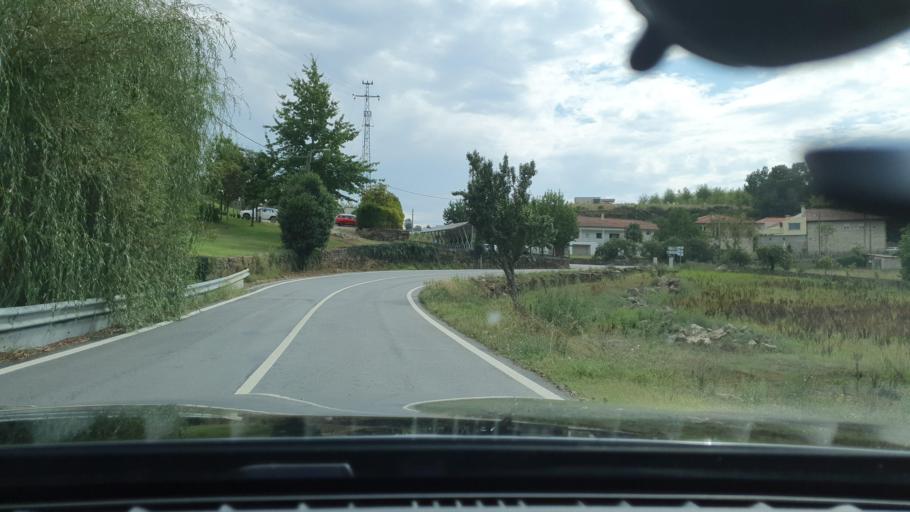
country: PT
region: Vila Real
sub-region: Boticas
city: Boticas
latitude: 41.7104
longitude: -7.5677
